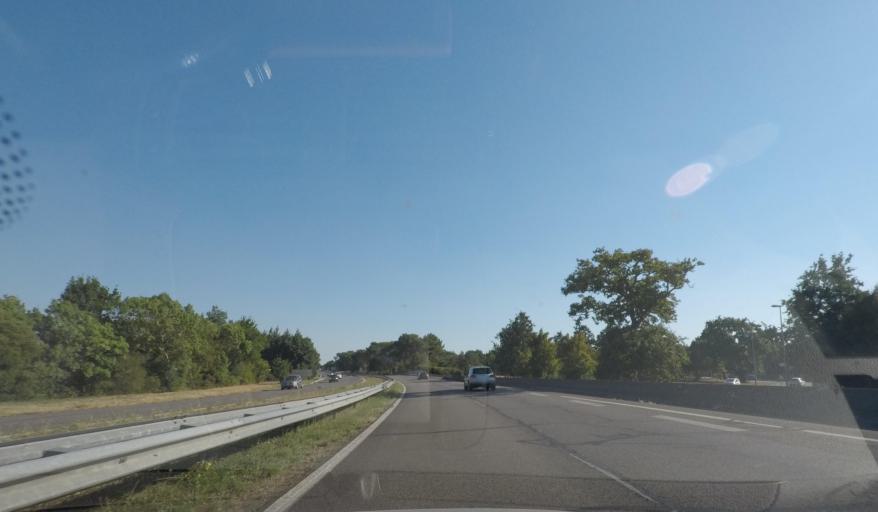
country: FR
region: Pays de la Loire
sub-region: Departement de la Loire-Atlantique
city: Saint-Brevin-les-Pins
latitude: 47.2362
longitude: -2.1577
